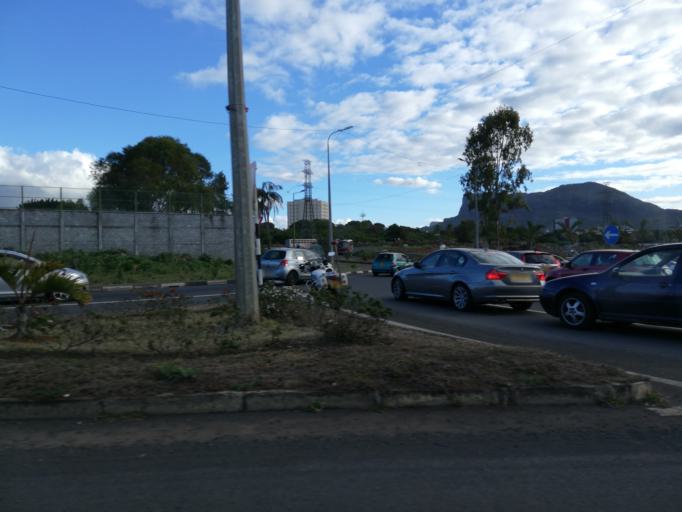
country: MU
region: Plaines Wilhems
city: Ebene
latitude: -20.2390
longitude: 57.4808
